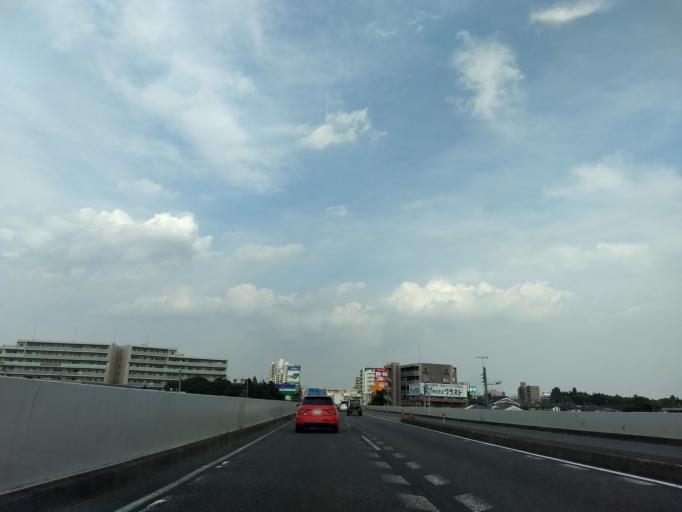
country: JP
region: Tokyo
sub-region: Machida-shi
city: Machida
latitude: 35.5140
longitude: 139.4619
